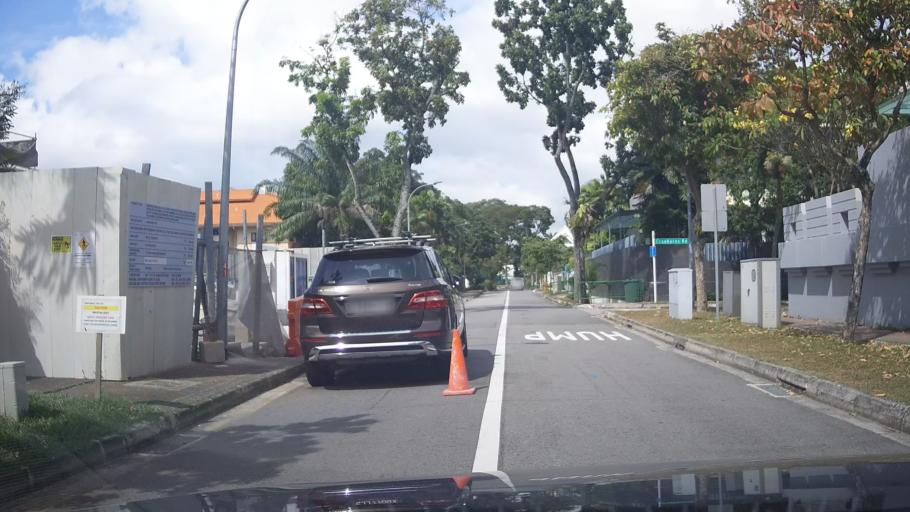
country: SG
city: Singapore
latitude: 1.3042
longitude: 103.8877
